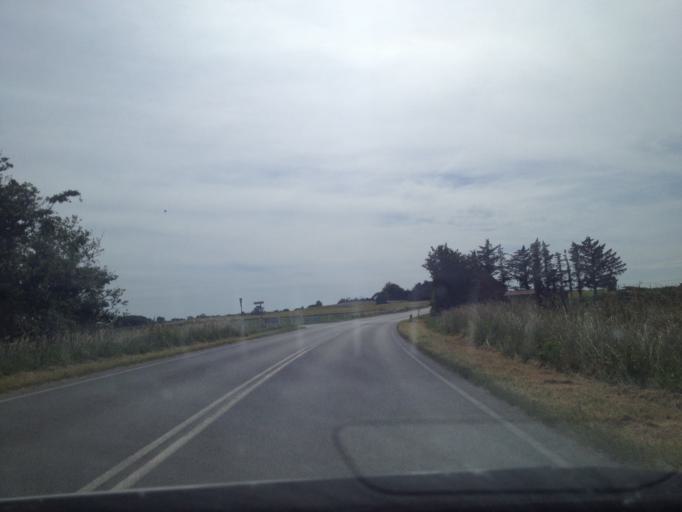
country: DK
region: Central Jutland
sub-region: Samso Kommune
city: Tranebjerg
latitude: 55.8081
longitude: 10.5785
